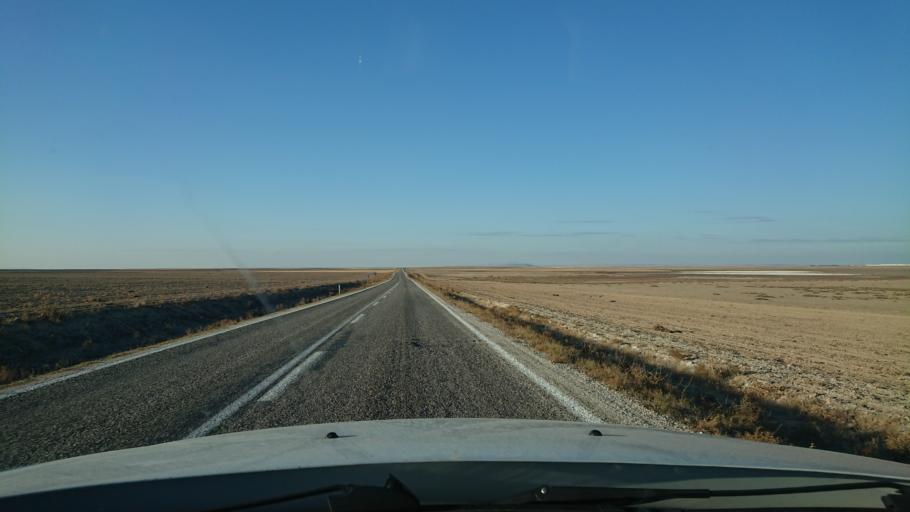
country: TR
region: Konya
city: Cihanbeyli
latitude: 38.7031
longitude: 33.1048
